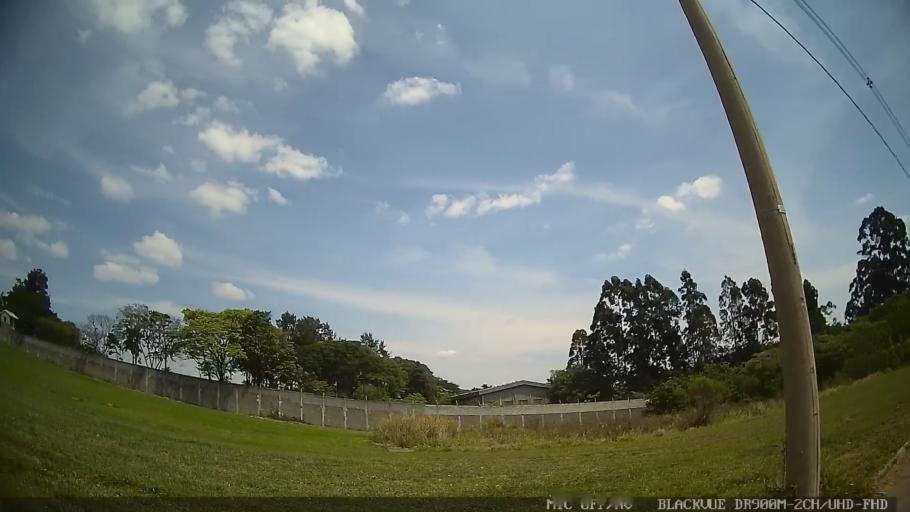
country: BR
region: Sao Paulo
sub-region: Itupeva
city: Itupeva
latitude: -23.2490
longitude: -47.0504
